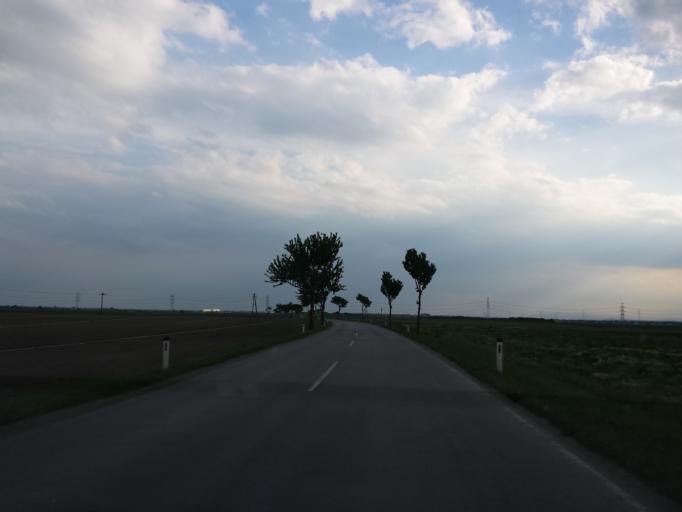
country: AT
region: Lower Austria
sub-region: Politischer Bezirk Ganserndorf
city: Raasdorf
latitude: 48.2324
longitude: 16.5811
